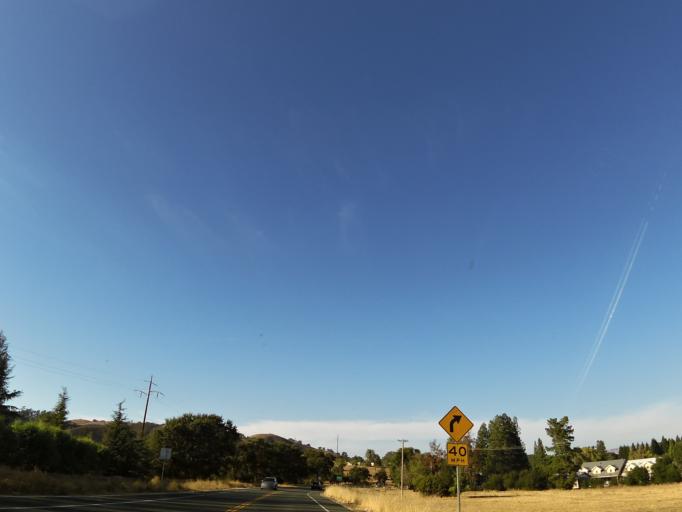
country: US
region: California
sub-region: Santa Clara County
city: San Martin
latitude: 37.0852
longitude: -121.6535
